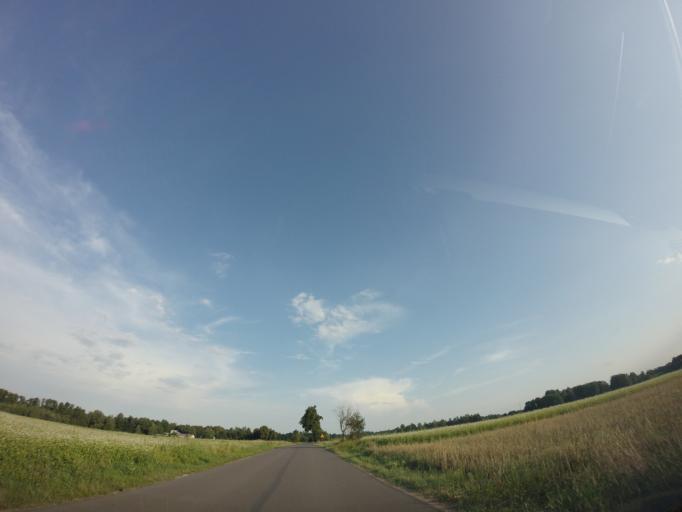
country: PL
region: Lublin Voivodeship
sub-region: Powiat pulawski
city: Kurow
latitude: 51.4289
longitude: 22.2171
